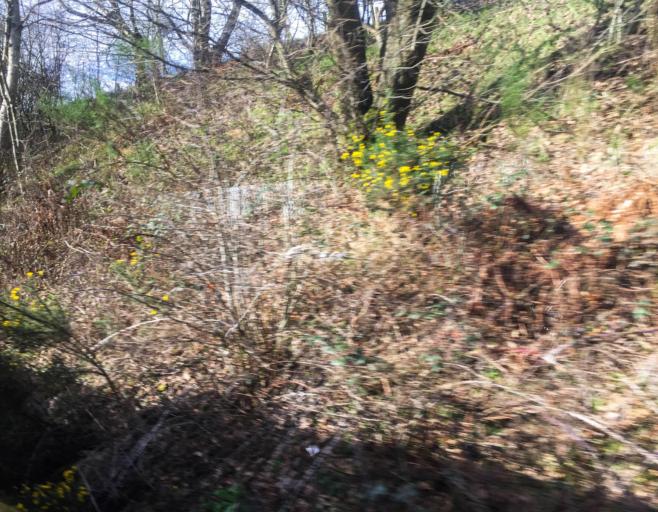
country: GB
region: Scotland
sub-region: East Dunbartonshire
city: Bearsden
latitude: 55.8943
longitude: -4.3120
